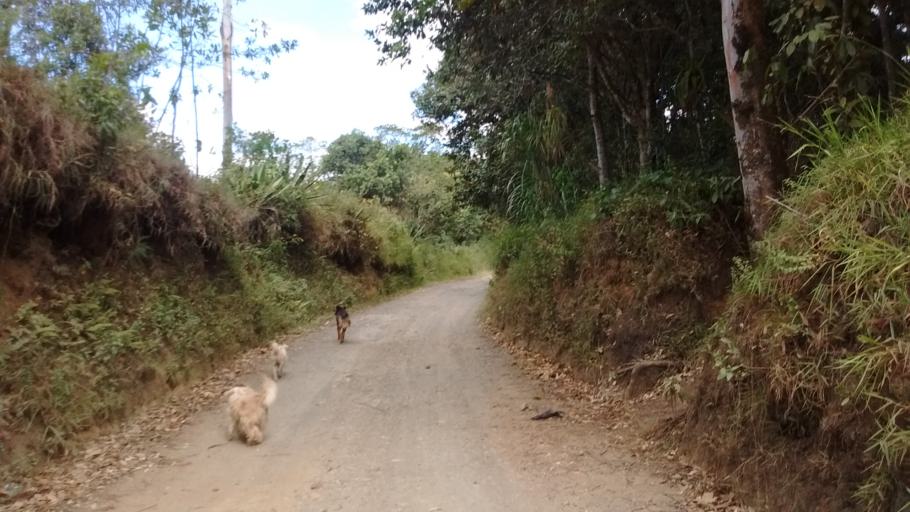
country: CO
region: Cauca
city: Popayan
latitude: 2.4933
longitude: -76.5878
